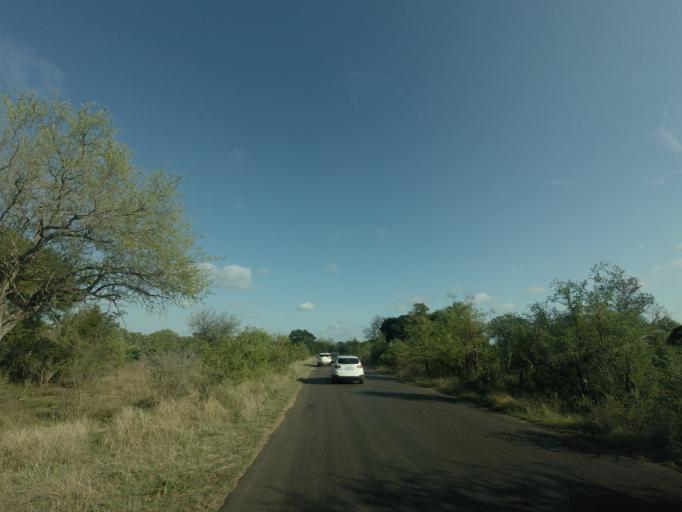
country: ZA
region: Mpumalanga
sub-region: Ehlanzeni District
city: Komatipoort
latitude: -25.2759
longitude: 31.8490
